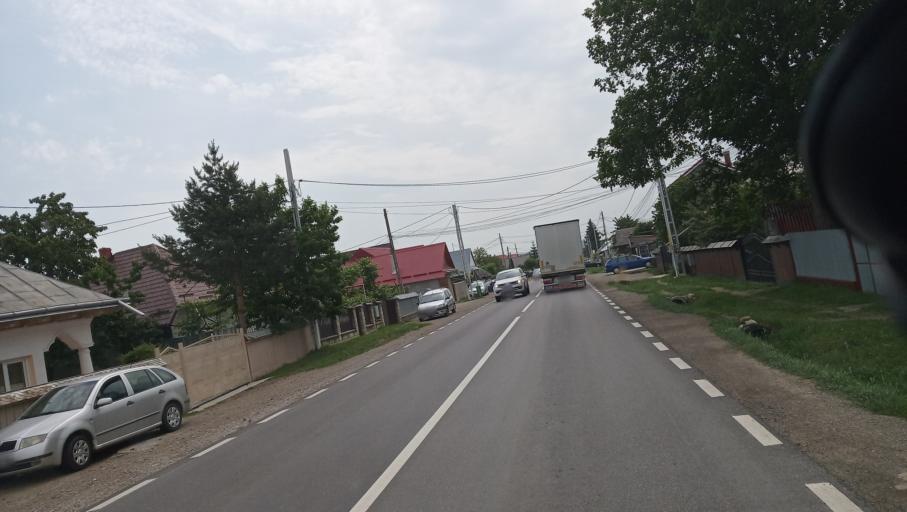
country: RO
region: Neamt
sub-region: Comuna Vanatori Neamt
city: Lunca
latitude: 47.2184
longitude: 26.3050
